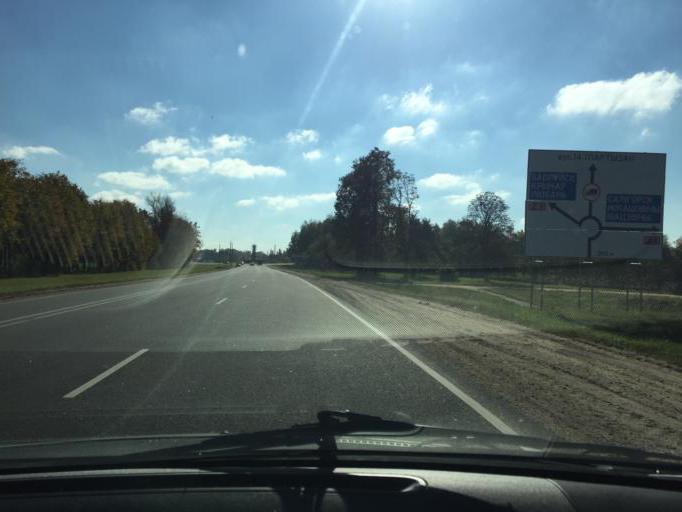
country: BY
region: Minsk
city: Slutsk
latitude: 53.0557
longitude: 27.5536
